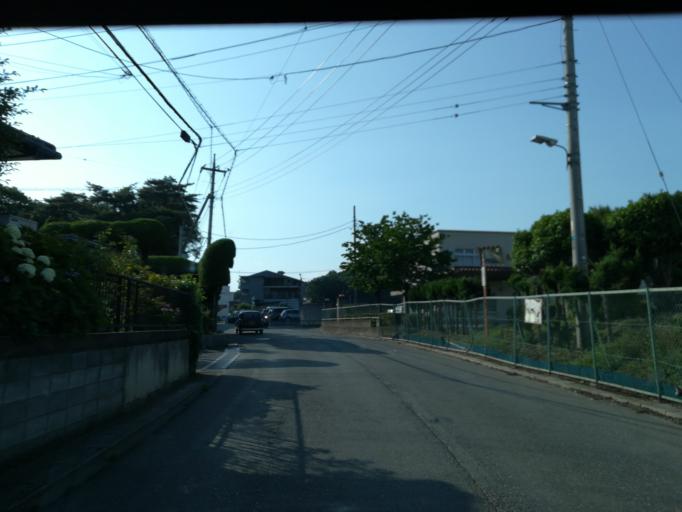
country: JP
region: Saitama
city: Sayama
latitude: 35.8040
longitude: 139.3826
